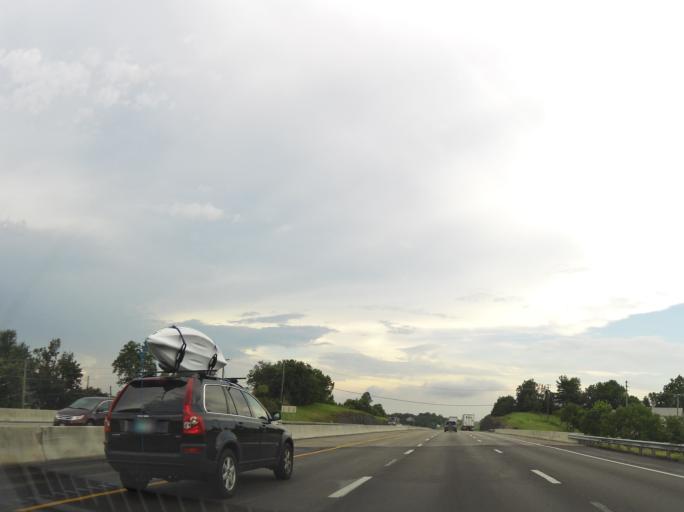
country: US
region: Kentucky
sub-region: Madison County
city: Richmond
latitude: 37.6992
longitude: -84.3173
